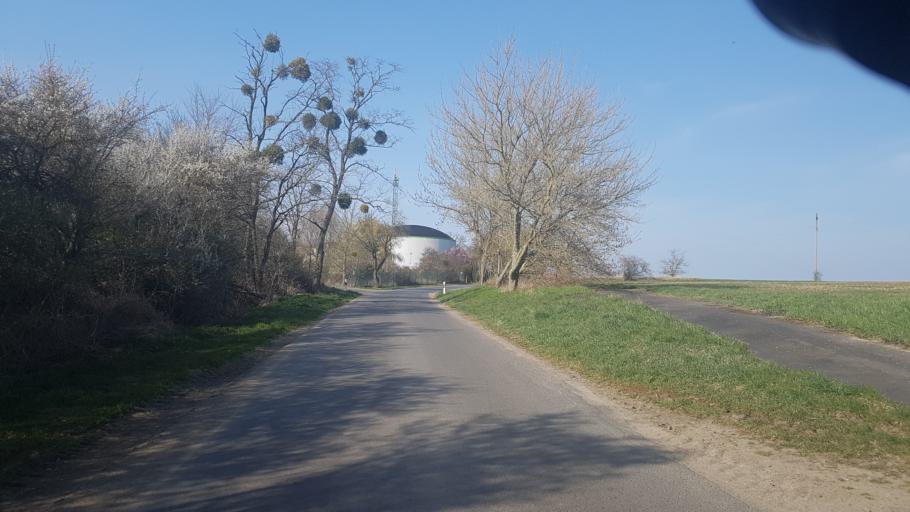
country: DE
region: Brandenburg
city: Gerswalde
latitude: 53.1882
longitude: 13.7793
